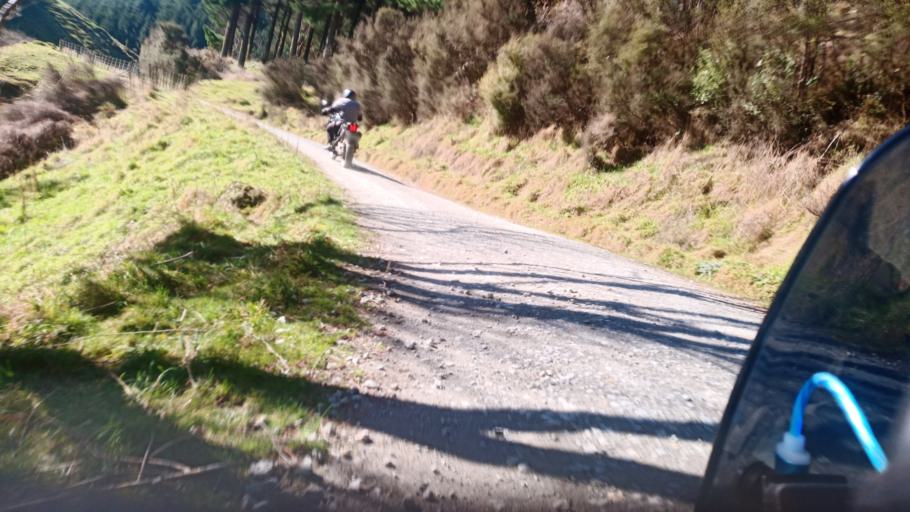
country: NZ
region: Hawke's Bay
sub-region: Wairoa District
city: Wairoa
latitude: -38.6586
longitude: 177.4904
